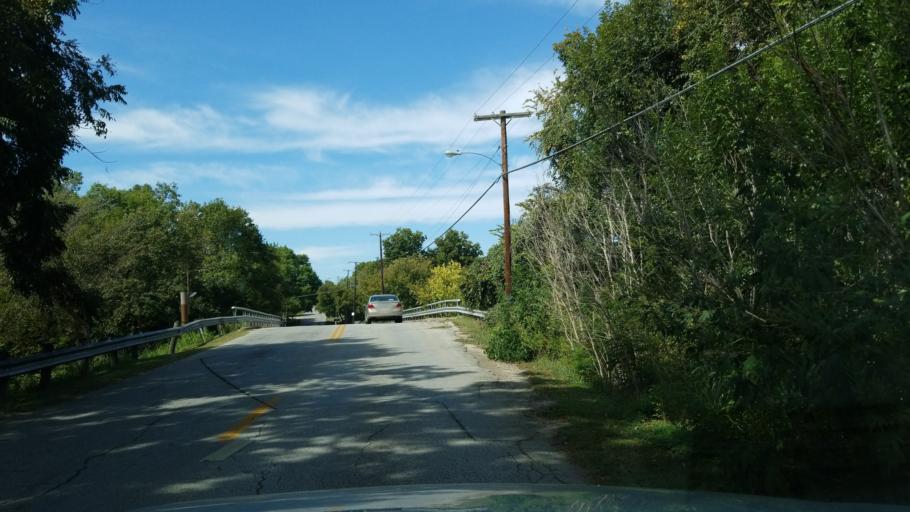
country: US
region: Texas
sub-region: Dallas County
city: Highland Park
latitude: 32.8049
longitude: -96.7175
